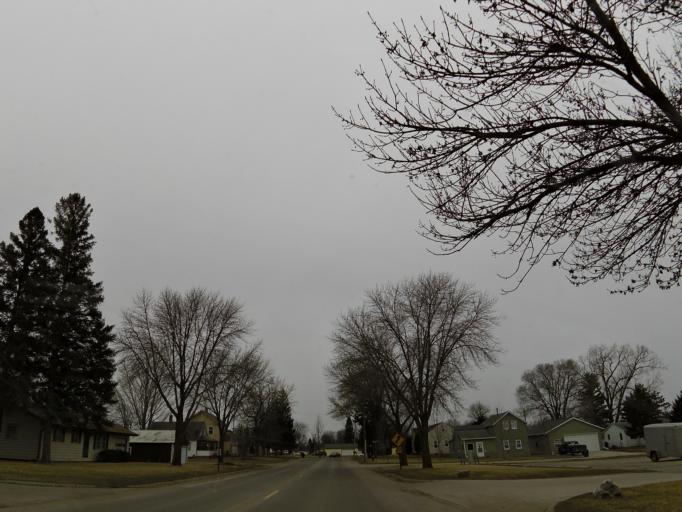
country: US
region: Minnesota
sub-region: Le Sueur County
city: Le Sueur
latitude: 44.4693
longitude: -93.9050
